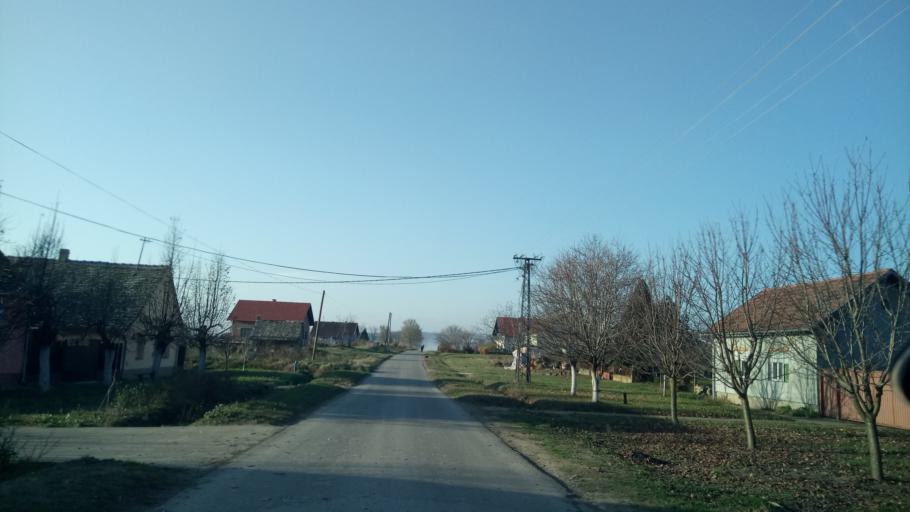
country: RS
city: Novi Slankamen
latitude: 45.1317
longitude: 20.2345
